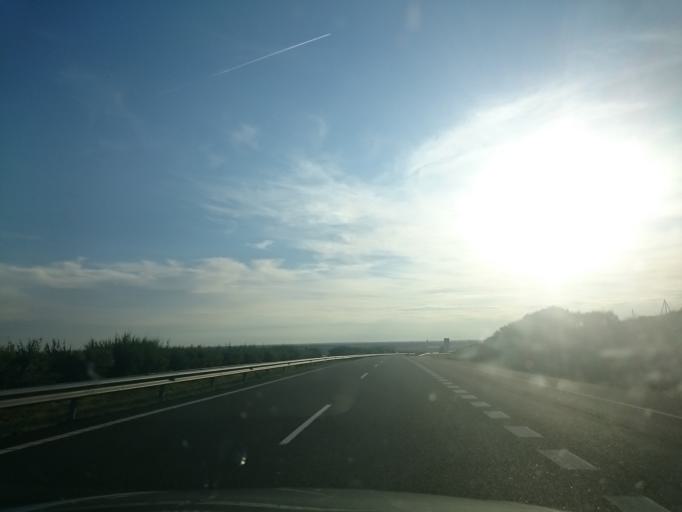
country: ES
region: Castille and Leon
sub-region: Provincia de Palencia
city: Moratinos
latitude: 42.3663
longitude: -4.9740
